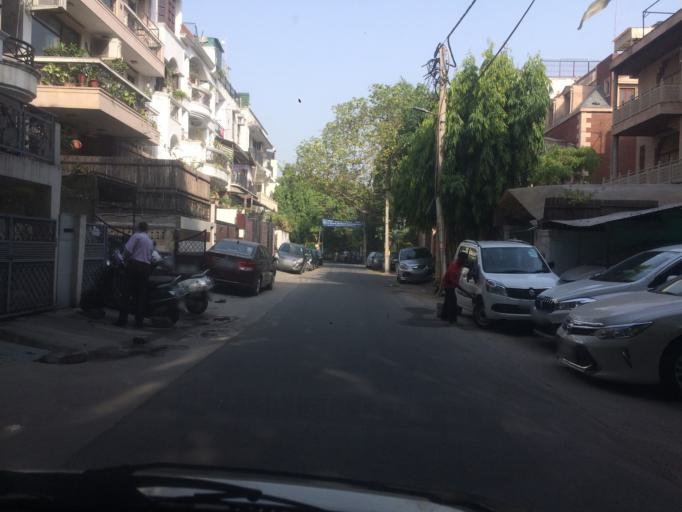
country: IN
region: NCT
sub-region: New Delhi
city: New Delhi
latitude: 28.5582
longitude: 77.2336
